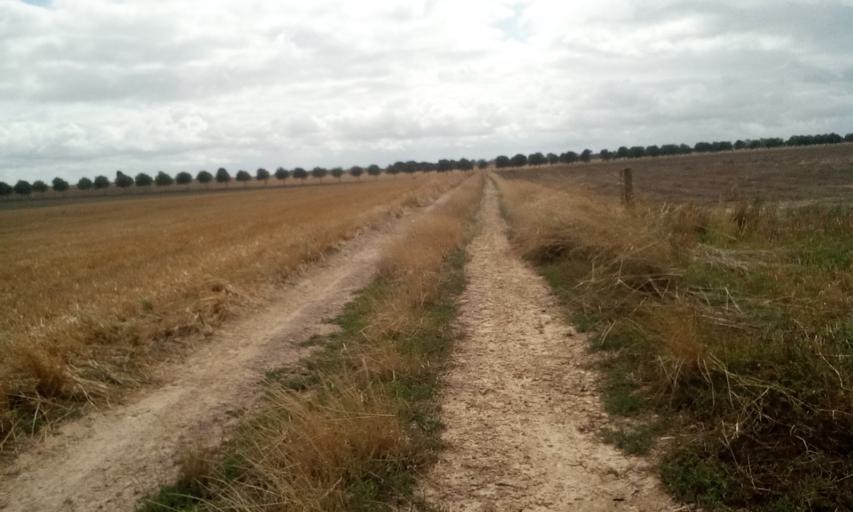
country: FR
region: Lower Normandy
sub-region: Departement du Calvados
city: Cheux
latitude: 49.1794
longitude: -0.5430
